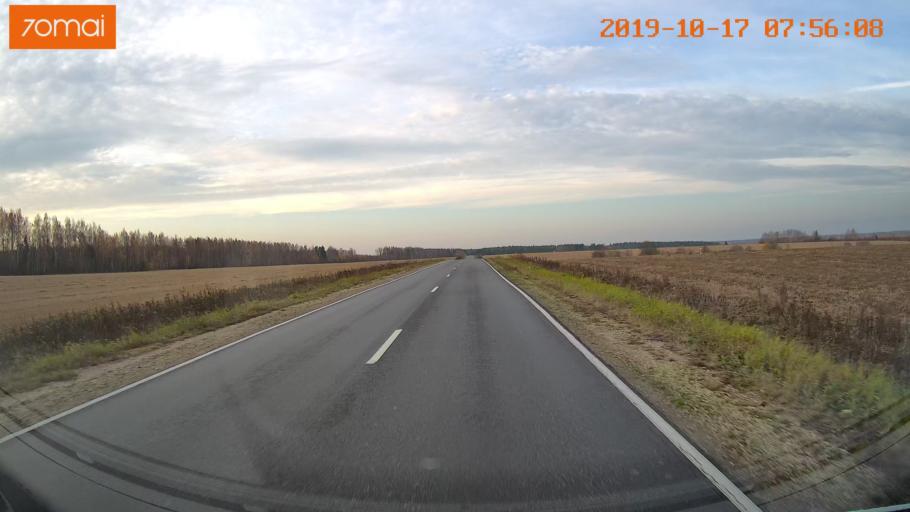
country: RU
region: Vladimir
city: Bavleny
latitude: 56.4268
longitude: 39.5940
